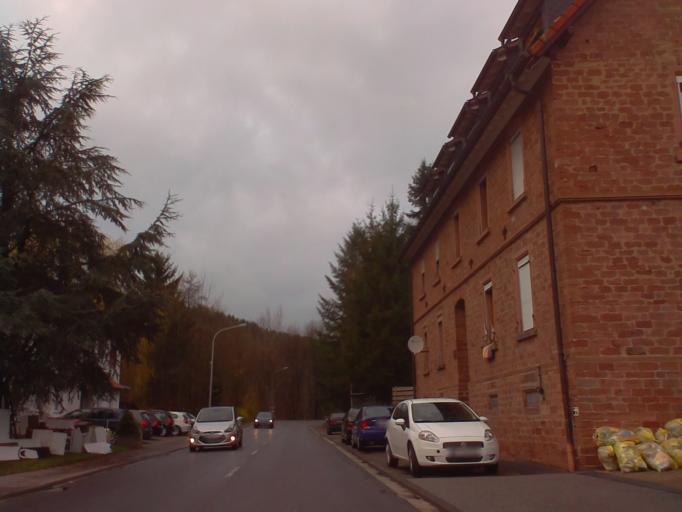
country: DE
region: Hesse
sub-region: Regierungsbezirk Darmstadt
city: Wald-Michelbach
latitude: 49.5642
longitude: 8.8465
